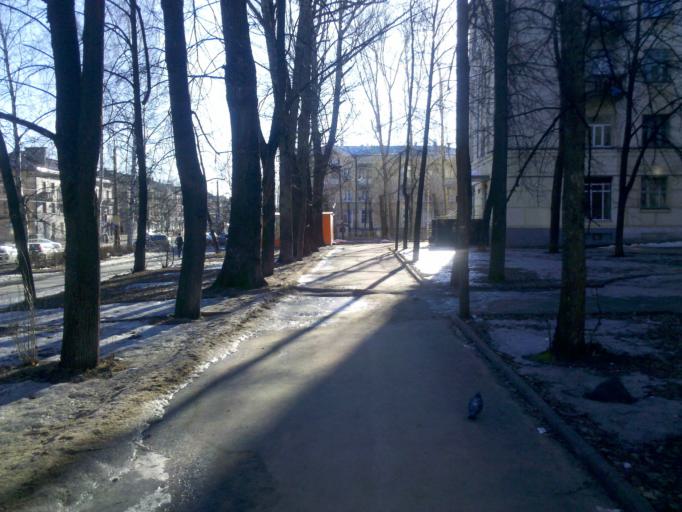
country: RU
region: Republic of Karelia
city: Petrozavodsk
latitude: 61.7989
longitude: 34.3267
